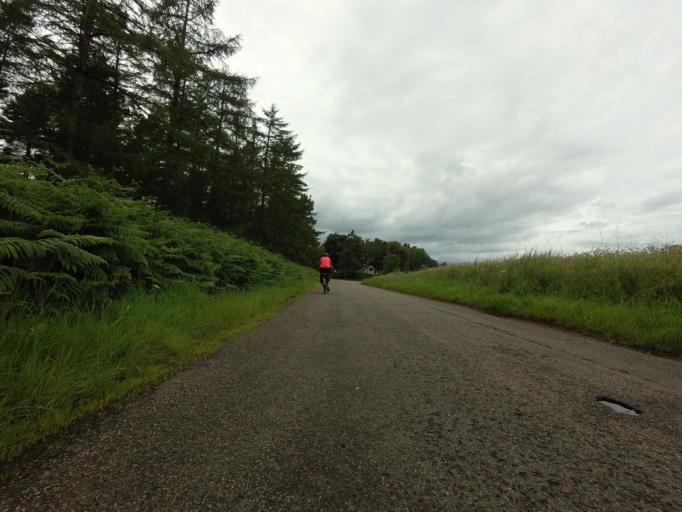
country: GB
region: Scotland
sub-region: Moray
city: Forres
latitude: 57.6038
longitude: -3.7449
